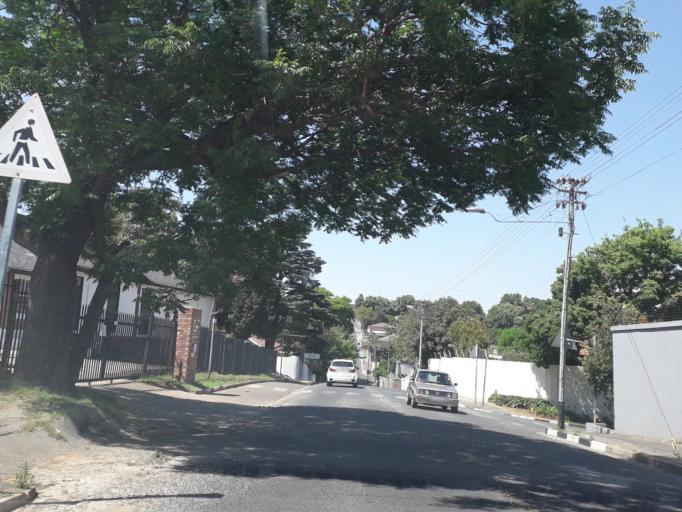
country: ZA
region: Gauteng
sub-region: City of Johannesburg Metropolitan Municipality
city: Johannesburg
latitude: -26.1375
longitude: 28.0241
